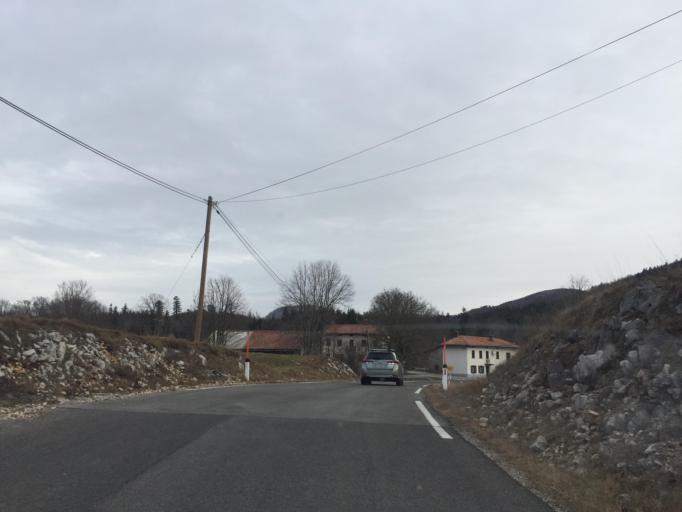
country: SI
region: Nova Gorica
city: Sempas
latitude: 45.9898
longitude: 13.7694
